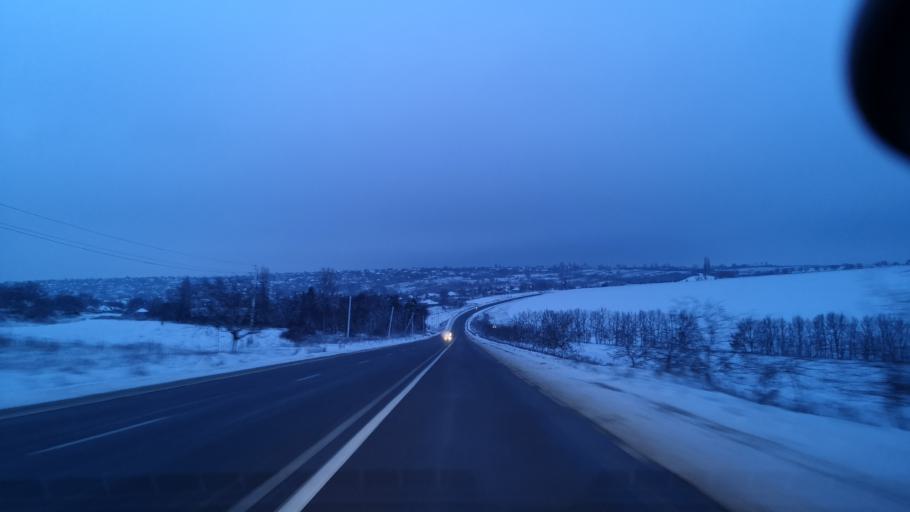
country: MD
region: Soldanesti
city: Soldanesti
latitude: 47.7096
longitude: 28.8472
